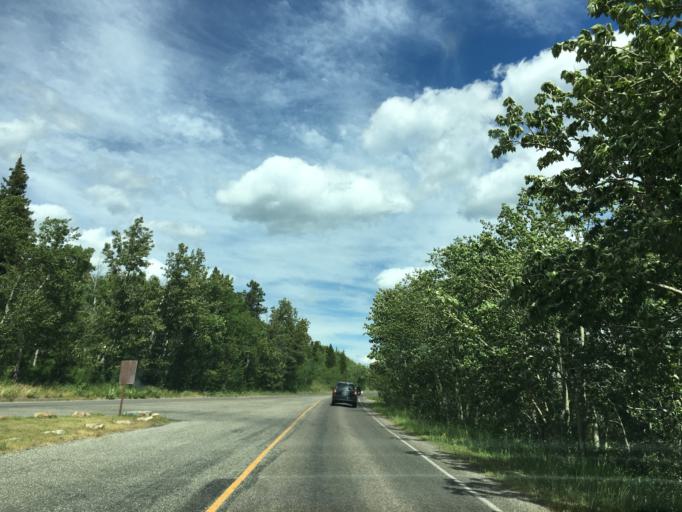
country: CA
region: Alberta
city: Cardston
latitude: 48.8222
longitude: -113.5793
